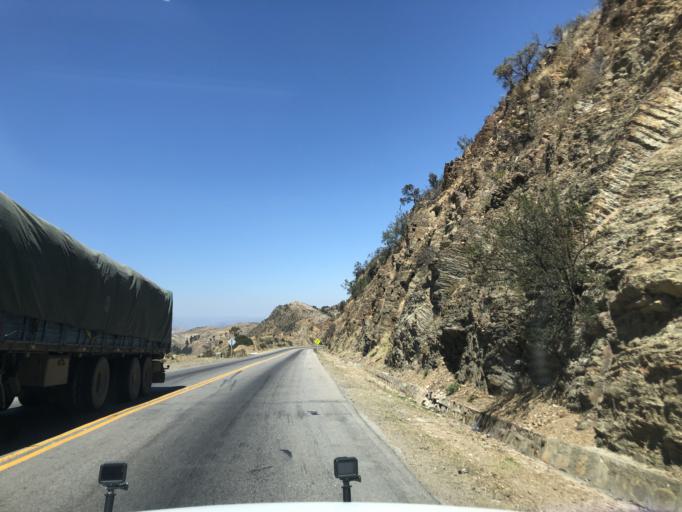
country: BO
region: Cochabamba
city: Irpa Irpa
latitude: -17.6661
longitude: -66.4441
